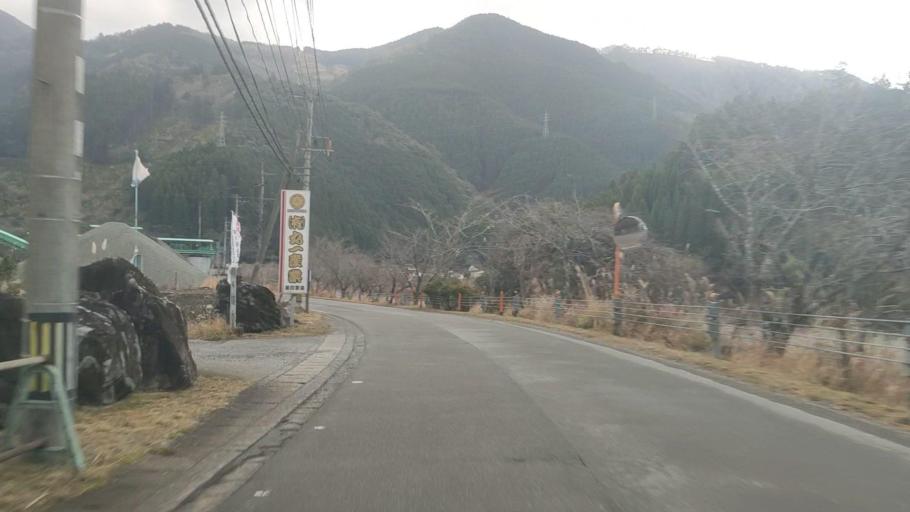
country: JP
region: Kumamoto
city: Hitoyoshi
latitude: 32.4367
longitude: 130.8573
